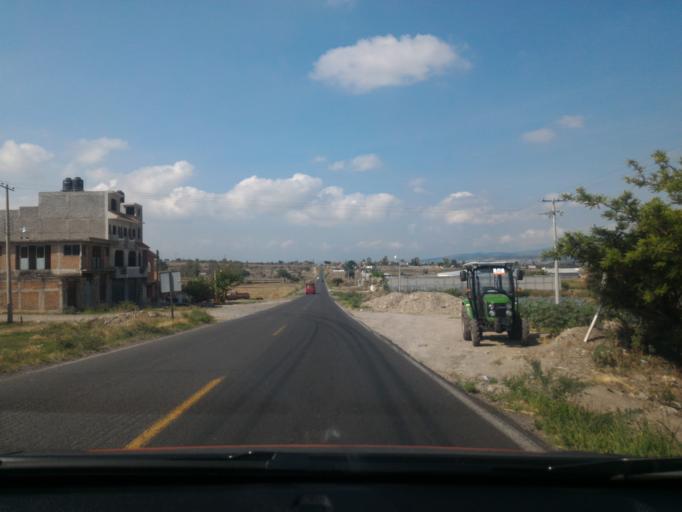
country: MX
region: Guanajuato
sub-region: Penjamo
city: Estacion la Piedad
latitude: 20.4206
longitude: -101.9939
